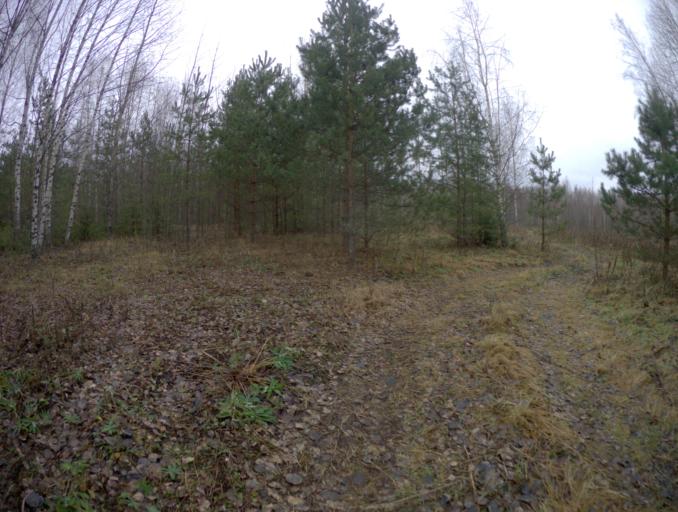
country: RU
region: Vladimir
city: Golovino
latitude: 56.0019
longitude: 40.5435
